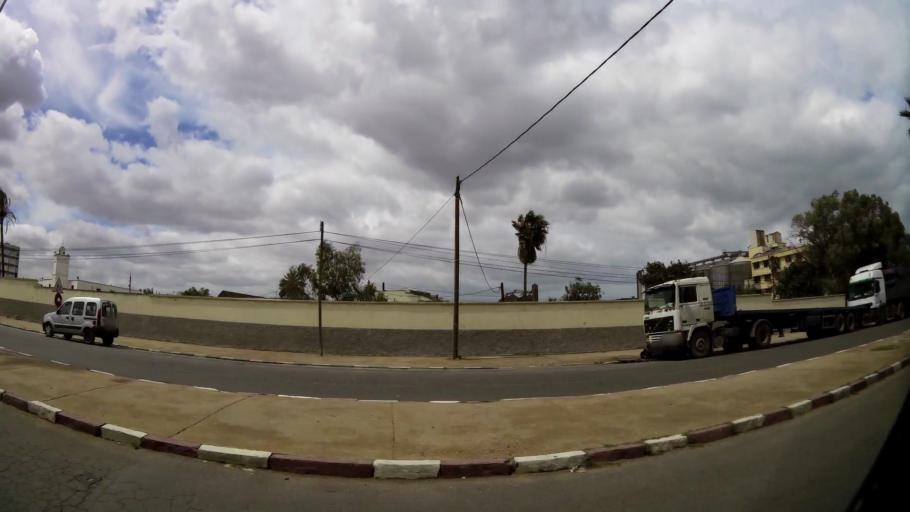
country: MA
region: Grand Casablanca
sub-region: Casablanca
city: Casablanca
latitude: 33.6059
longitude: -7.5633
